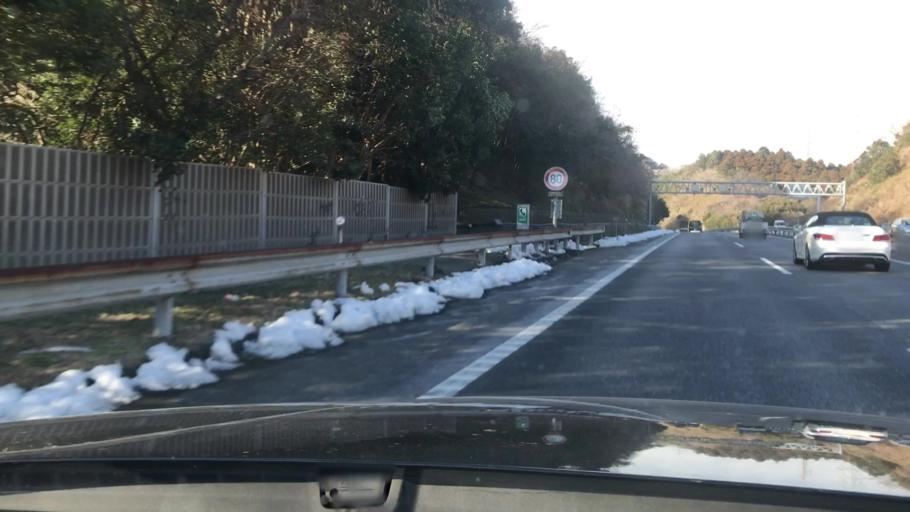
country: JP
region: Kanagawa
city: Zushi
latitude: 35.2970
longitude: 139.6173
